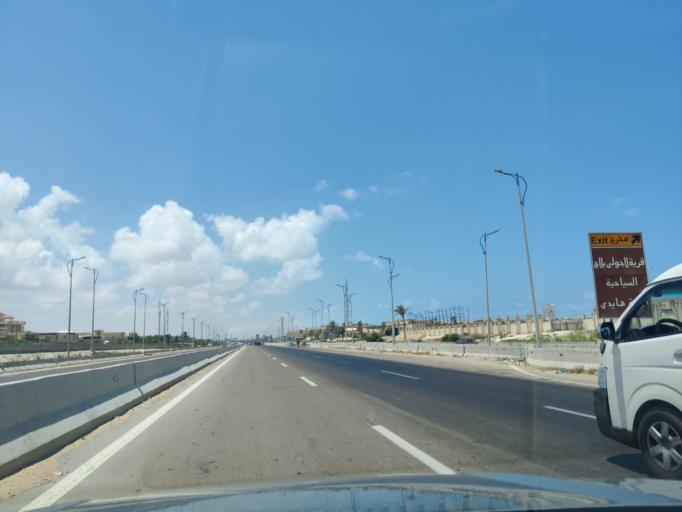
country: EG
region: Muhafazat Matruh
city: Al `Alamayn
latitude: 30.9029
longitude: 29.4200
